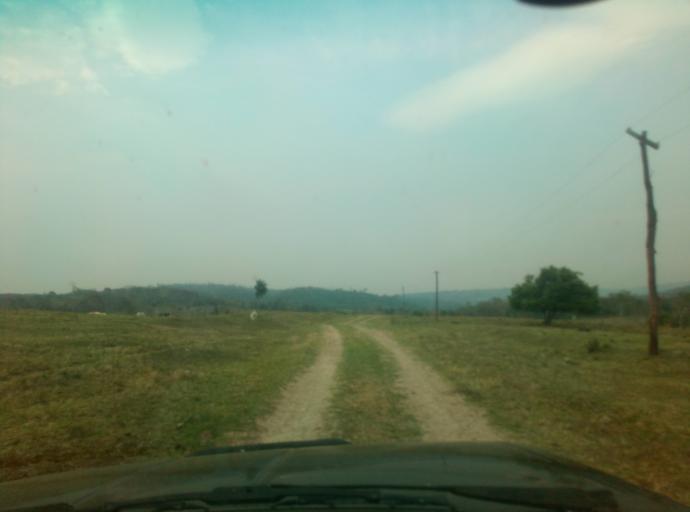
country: PY
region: Caaguazu
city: San Joaquin
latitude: -25.1034
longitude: -56.1257
